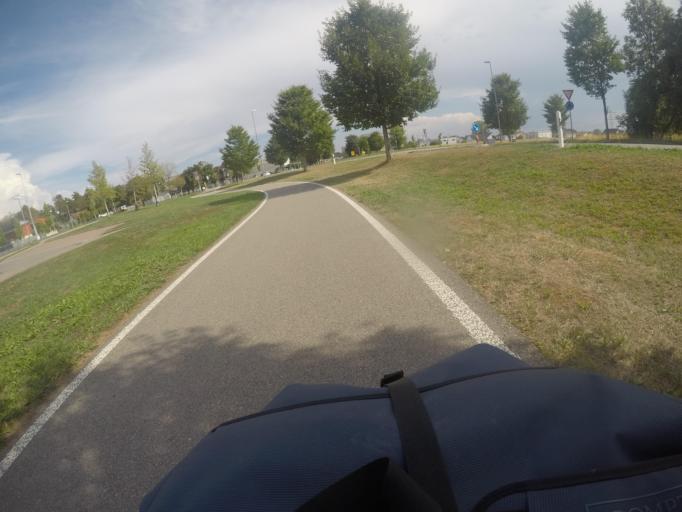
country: DE
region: Baden-Wuerttemberg
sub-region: Freiburg Region
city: Efringen-Kirchen
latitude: 47.6515
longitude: 7.5613
